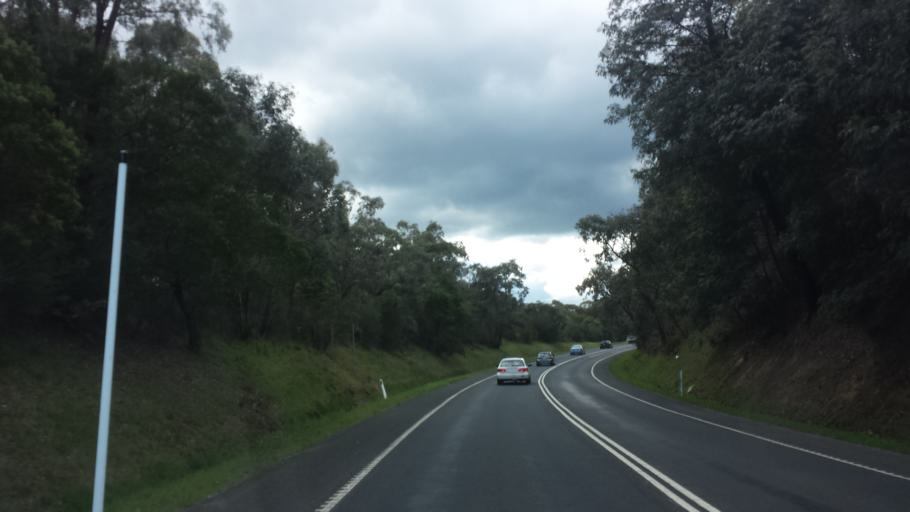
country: AU
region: Victoria
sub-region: Yarra Ranges
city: Selby
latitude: -37.9417
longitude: 145.3825
